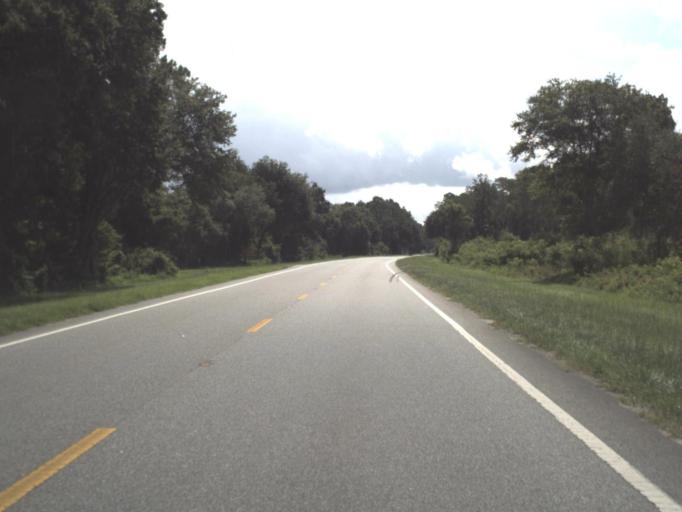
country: US
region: Florida
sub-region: Hernando County
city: Ridge Manor
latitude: 28.5075
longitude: -82.1490
